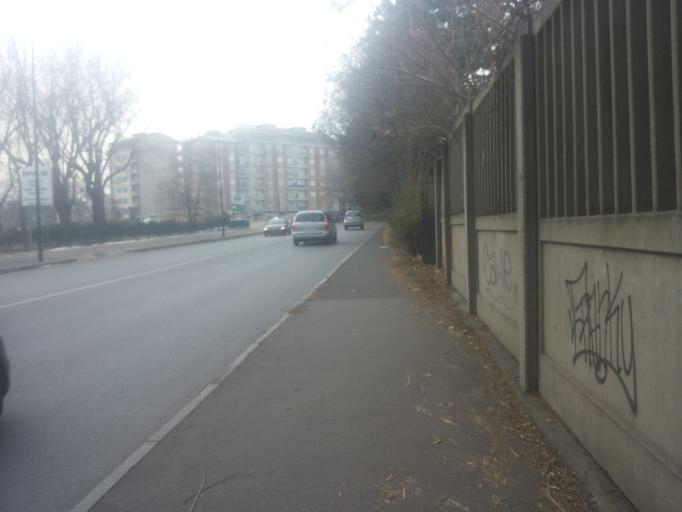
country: IT
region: Piedmont
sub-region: Provincia di Torino
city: Lesna
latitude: 45.0549
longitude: 7.6431
